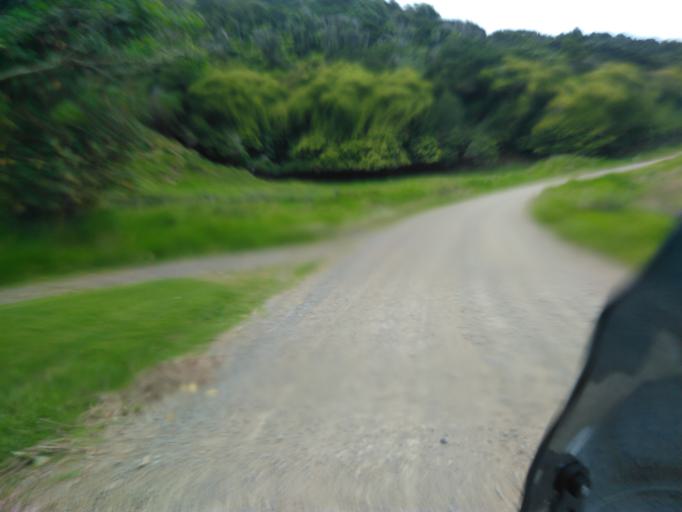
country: NZ
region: Bay of Plenty
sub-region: Opotiki District
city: Opotiki
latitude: -38.0133
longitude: 177.4205
